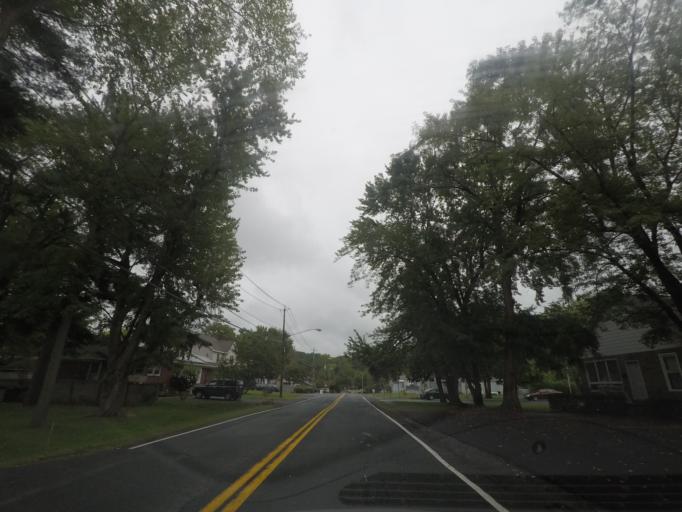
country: US
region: New York
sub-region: Rensselaer County
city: Hampton Manor
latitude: 42.6190
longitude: -73.7304
